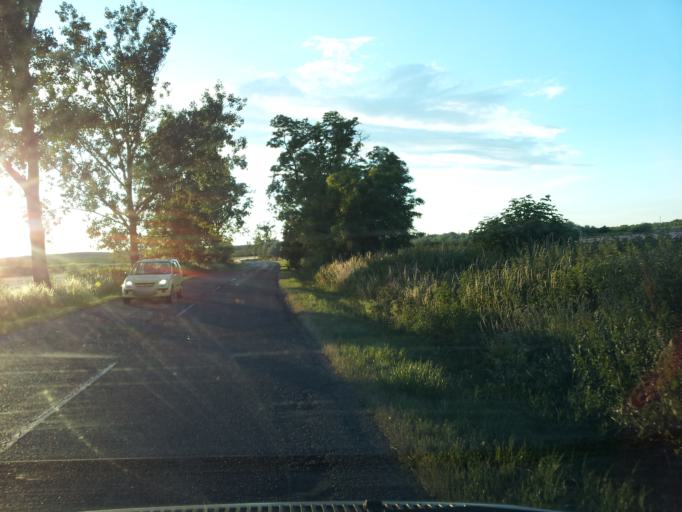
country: HU
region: Veszprem
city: Szentkiralyszabadja
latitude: 47.0307
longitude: 17.9357
